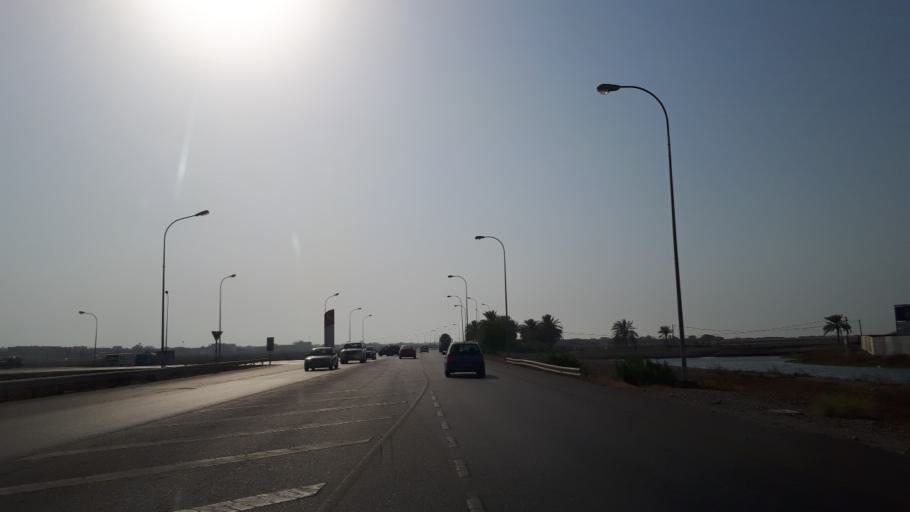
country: OM
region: Muhafazat Masqat
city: As Sib al Jadidah
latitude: 23.6260
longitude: 58.2625
